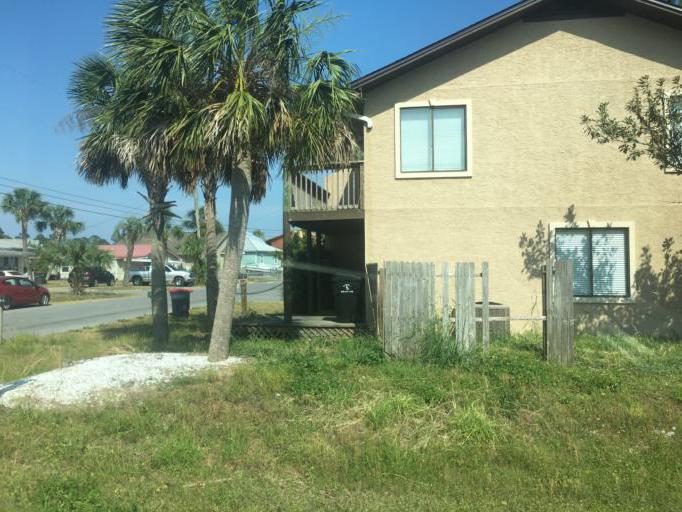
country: US
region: Florida
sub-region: Bay County
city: Panama City Beach
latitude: 30.1653
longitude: -85.7818
